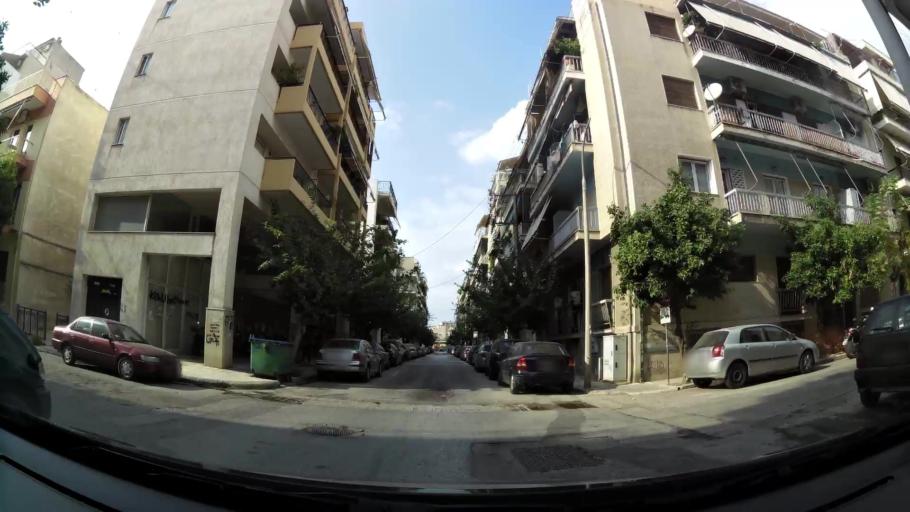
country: GR
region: Attica
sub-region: Nomarchia Athinas
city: Kallithea
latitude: 37.9616
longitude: 23.7063
